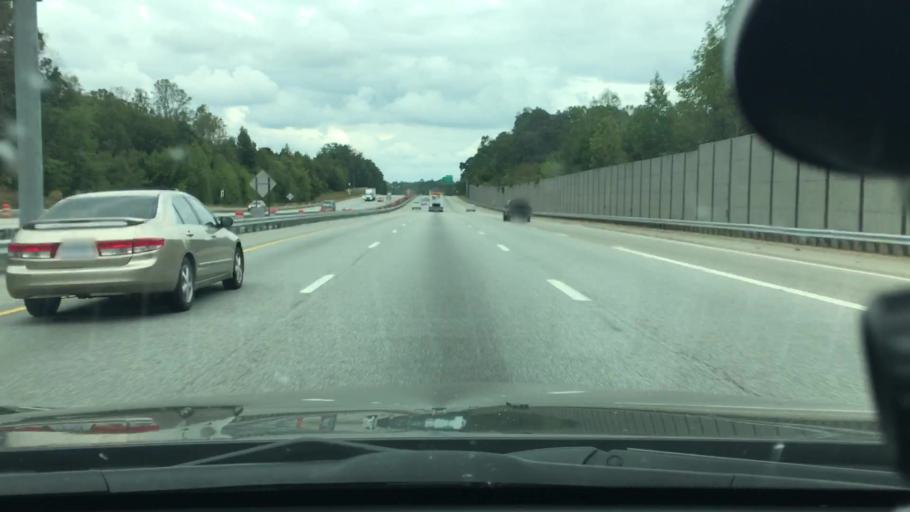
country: US
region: North Carolina
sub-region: Forsyth County
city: Clemmons
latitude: 36.0241
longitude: -80.4020
